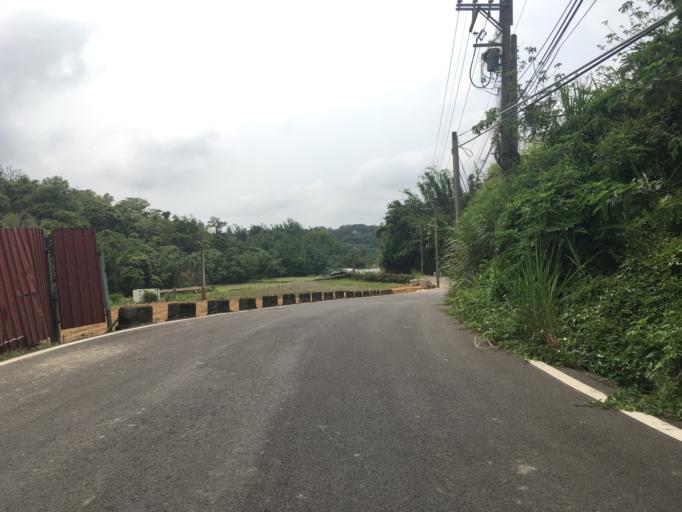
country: TW
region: Taiwan
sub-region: Hsinchu
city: Hsinchu
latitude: 24.7369
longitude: 120.9775
